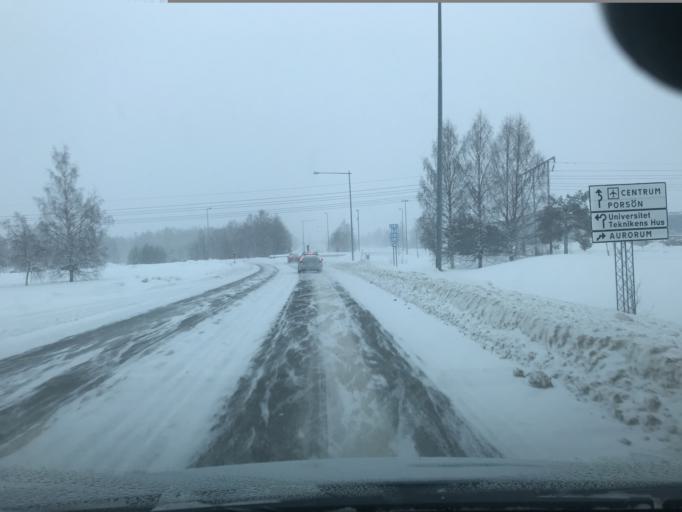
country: SE
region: Norrbotten
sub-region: Lulea Kommun
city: Lulea
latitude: 65.6167
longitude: 22.1313
